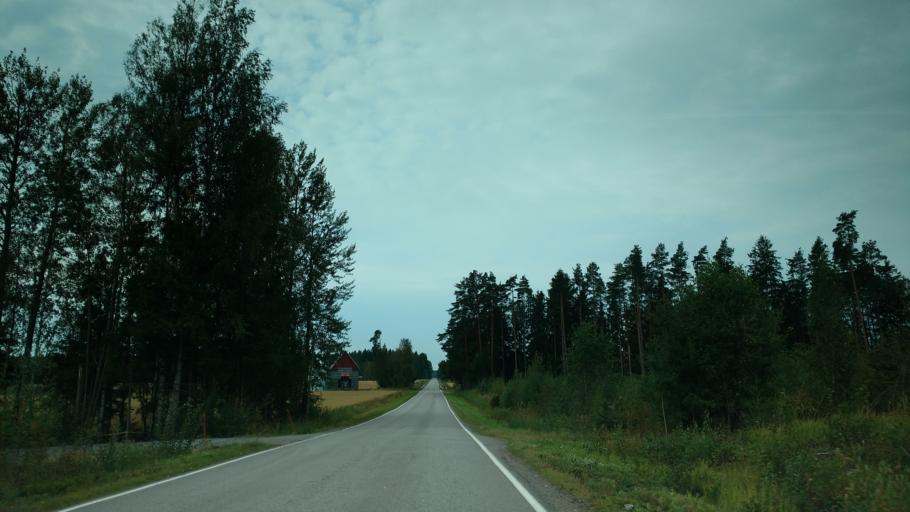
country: FI
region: Varsinais-Suomi
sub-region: Loimaa
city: Koski Tl
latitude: 60.7315
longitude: 23.1890
